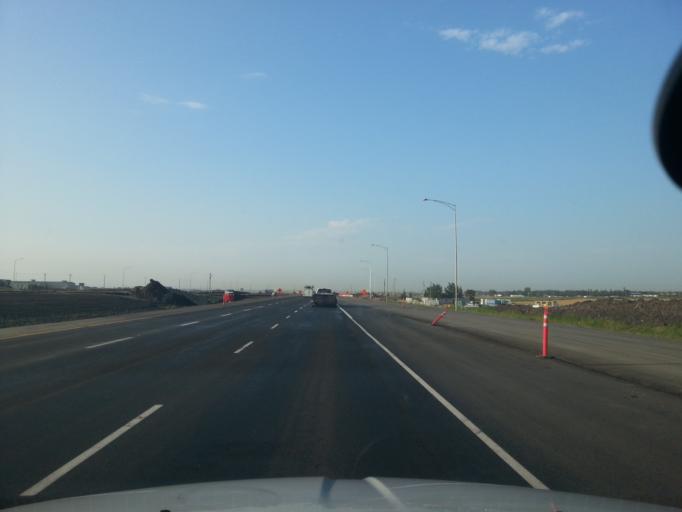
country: CA
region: Alberta
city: Beaumont
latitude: 53.3923
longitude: -113.5143
